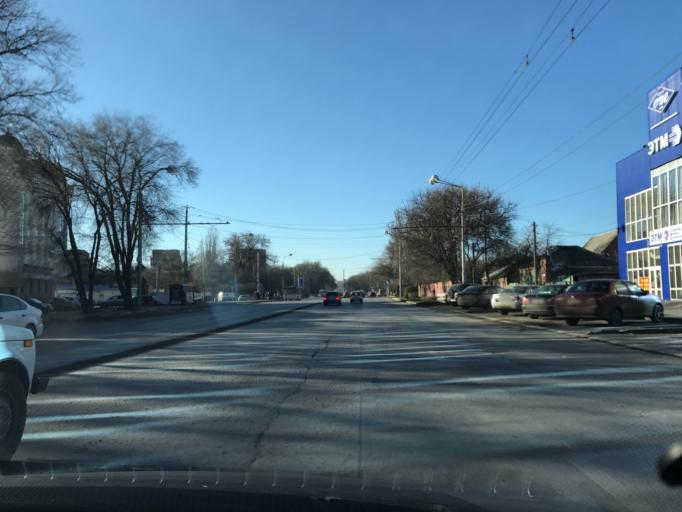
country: RU
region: Rostov
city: Rostov-na-Donu
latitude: 47.2122
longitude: 39.6491
